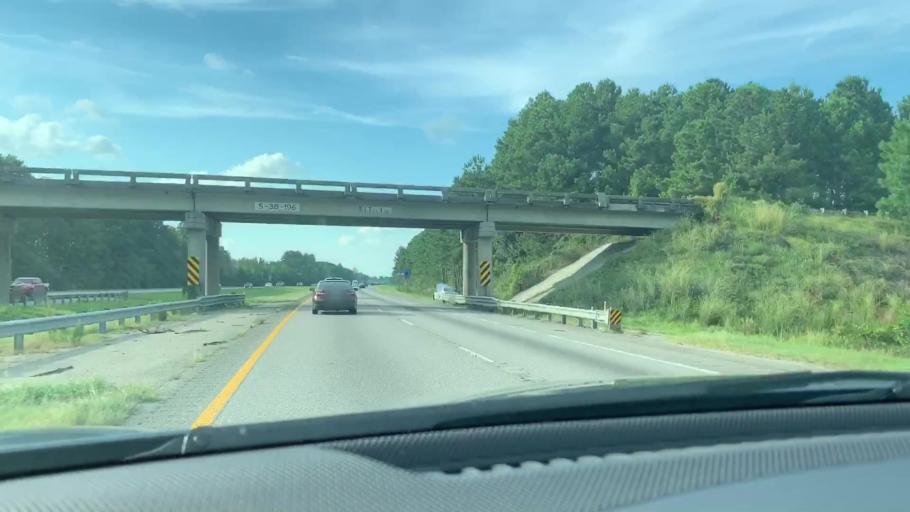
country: US
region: South Carolina
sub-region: Orangeburg County
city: Brookdale
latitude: 33.4503
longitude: -80.7207
